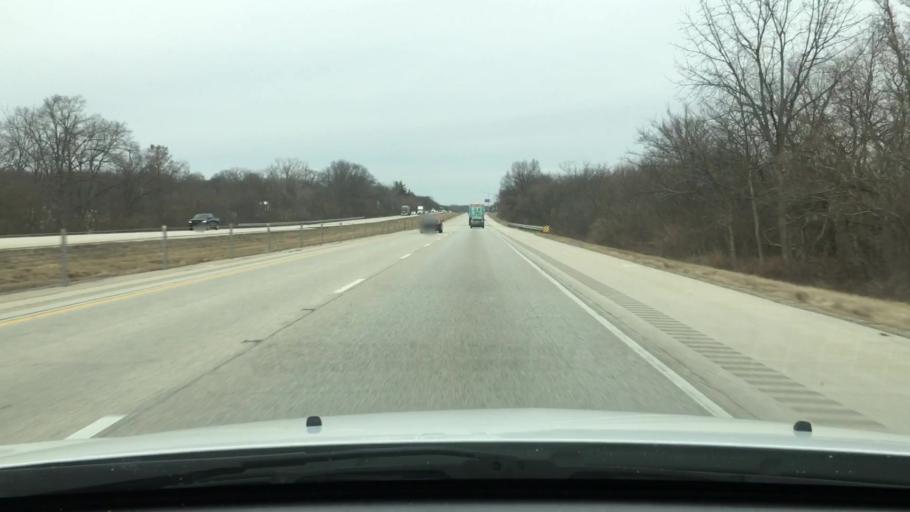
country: US
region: Illinois
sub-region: Sangamon County
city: Sherman
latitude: 39.8562
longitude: -89.5949
